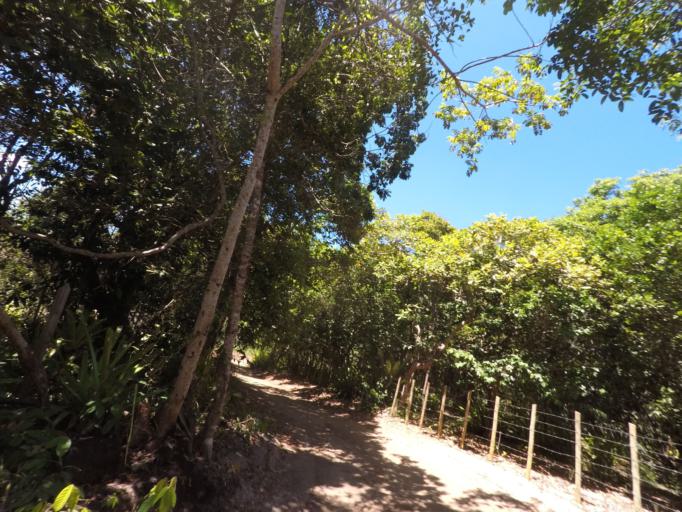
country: BR
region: Bahia
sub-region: Marau
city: Marau
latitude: -14.0262
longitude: -38.9501
